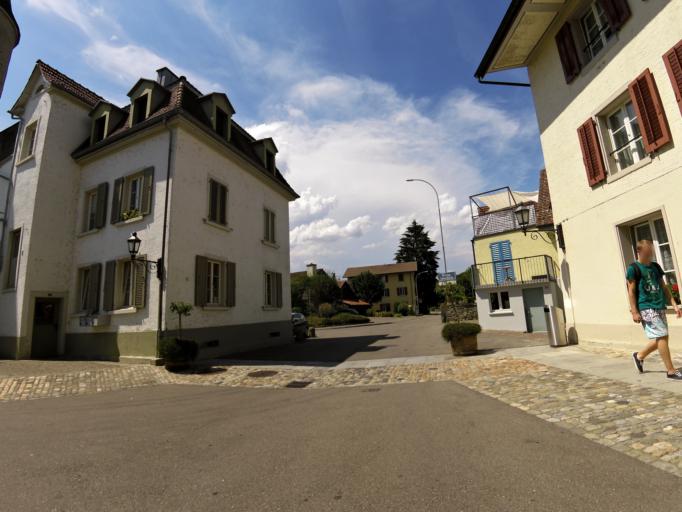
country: CH
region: Aargau
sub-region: Bezirk Baden
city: Mellingen
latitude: 47.4195
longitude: 8.2722
